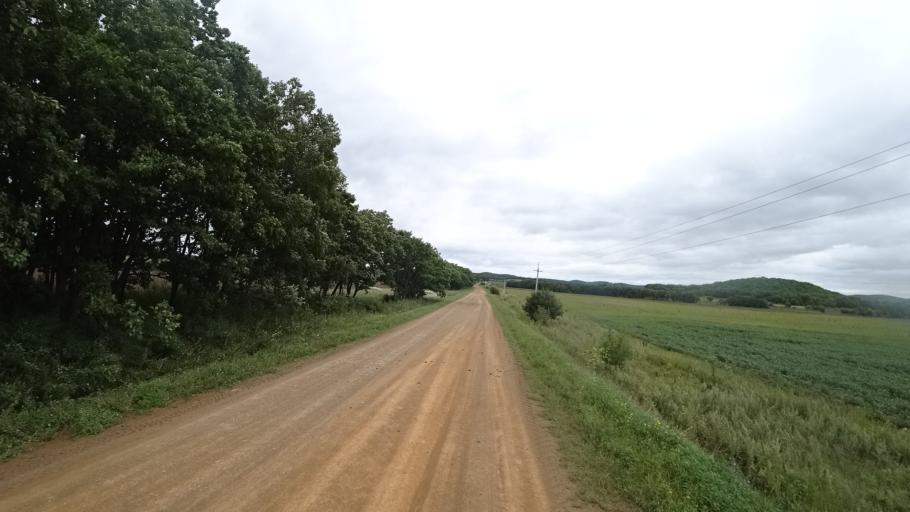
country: RU
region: Primorskiy
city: Chernigovka
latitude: 44.4415
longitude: 132.5947
